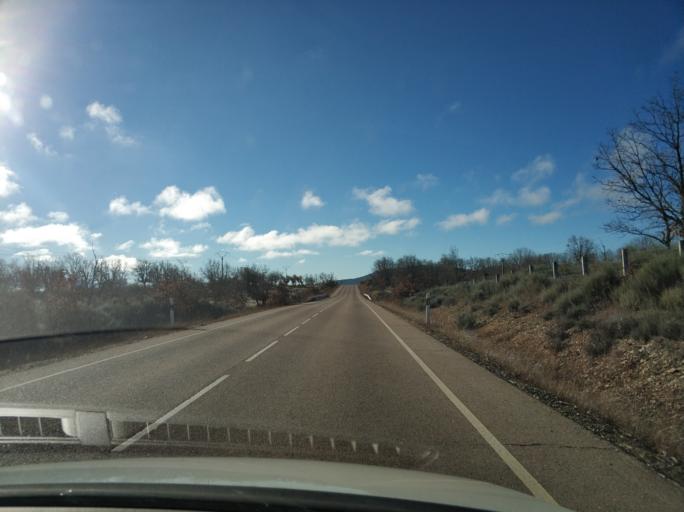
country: ES
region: Castille and Leon
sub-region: Provincia de Salamanca
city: Linares de Riofrio
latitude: 40.6241
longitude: -5.9070
